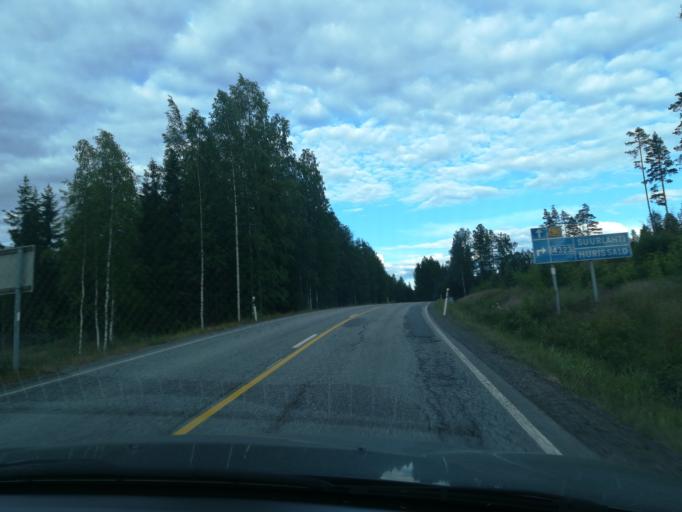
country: FI
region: South Karelia
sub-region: Lappeenranta
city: Savitaipale
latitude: 61.4993
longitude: 27.8245
